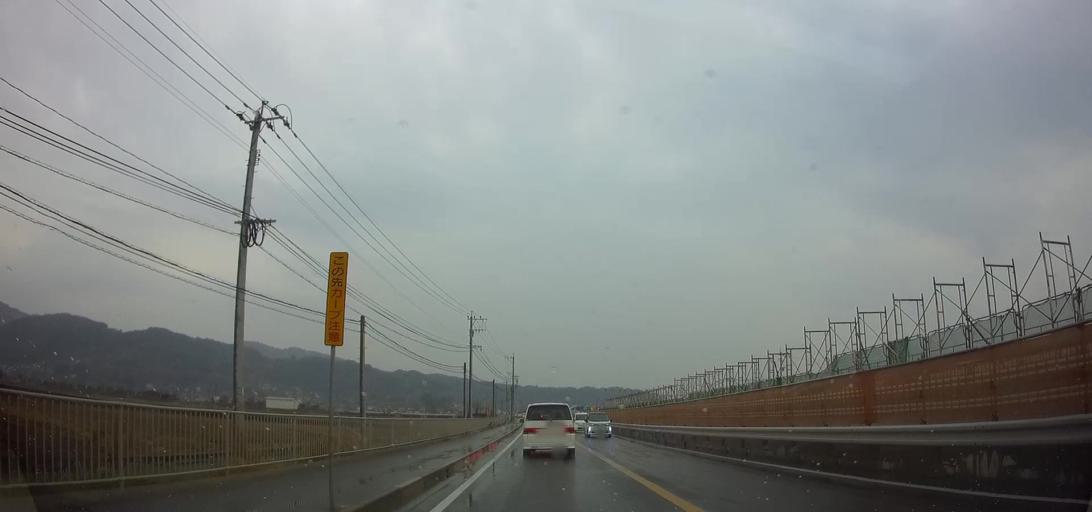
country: JP
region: Nagasaki
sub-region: Isahaya-shi
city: Isahaya
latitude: 32.8345
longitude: 130.1200
